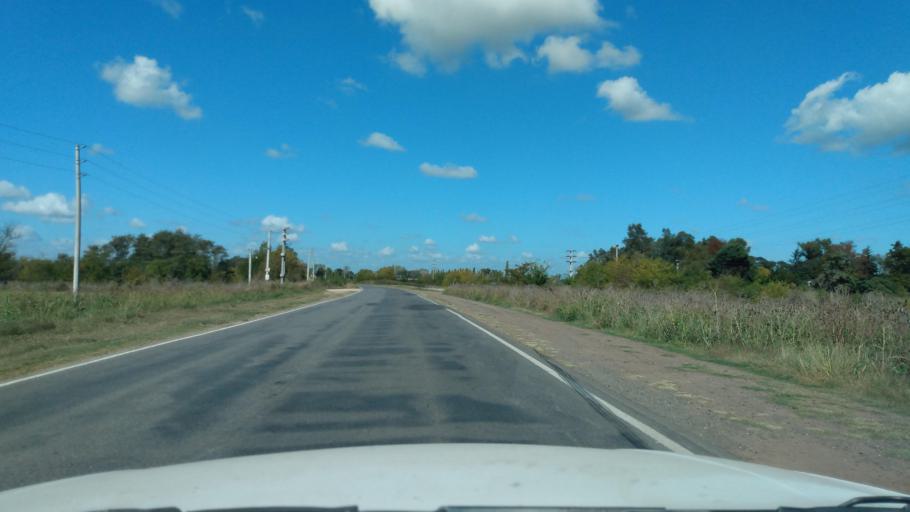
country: AR
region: Buenos Aires
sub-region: Partido de Mercedes
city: Mercedes
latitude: -34.7010
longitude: -59.4032
